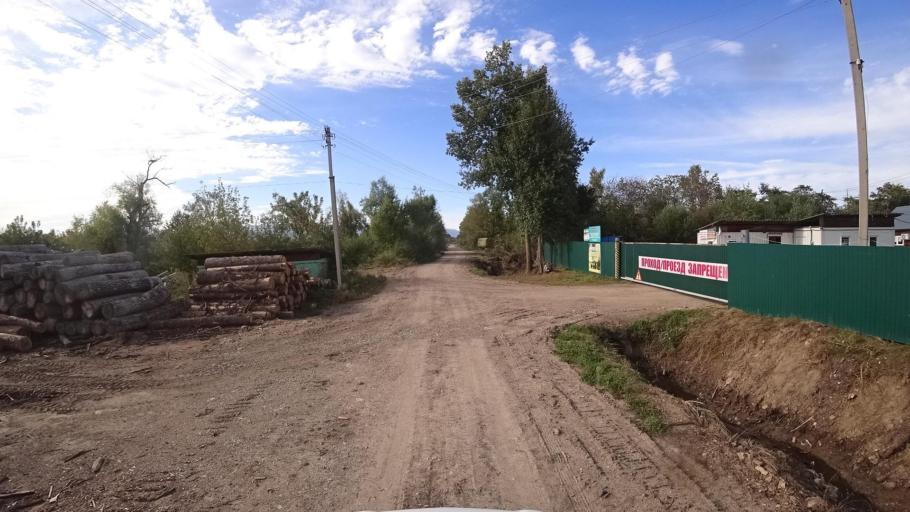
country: RU
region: Primorskiy
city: Dostoyevka
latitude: 44.3069
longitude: 133.4664
